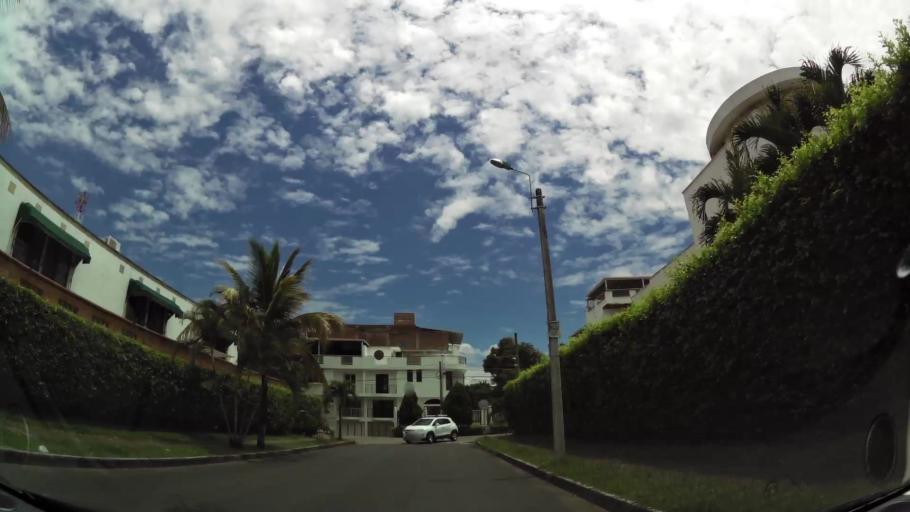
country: CO
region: Valle del Cauca
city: Cali
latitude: 3.3894
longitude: -76.5314
